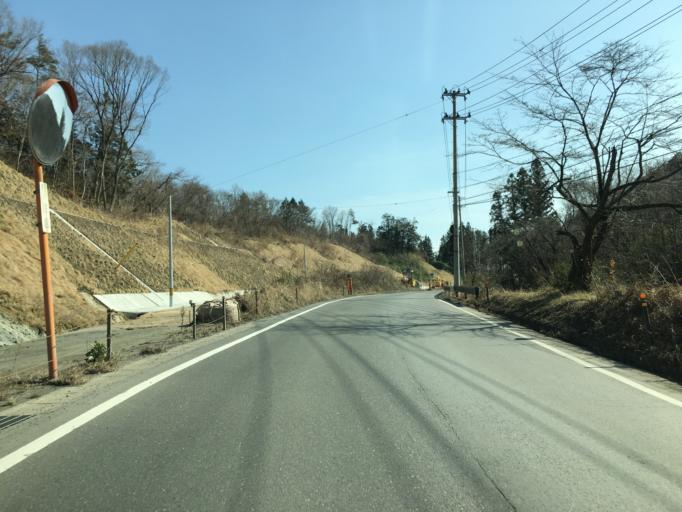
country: JP
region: Ibaraki
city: Daigo
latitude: 36.8495
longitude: 140.4321
